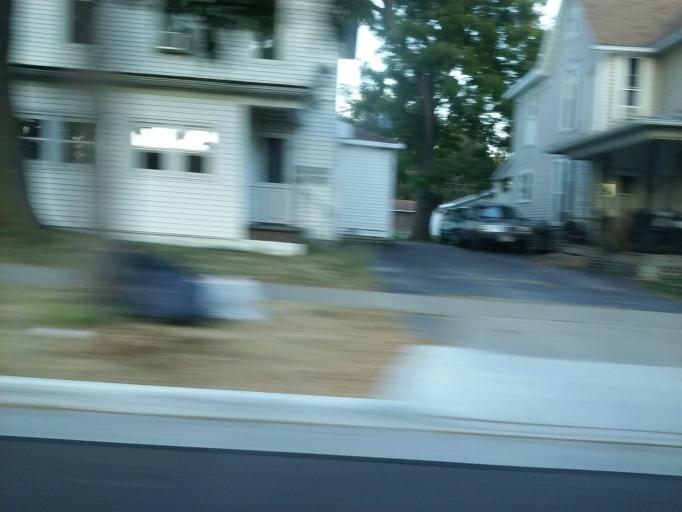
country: US
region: Ohio
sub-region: Hancock County
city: Findlay
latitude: 41.0484
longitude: -83.6501
